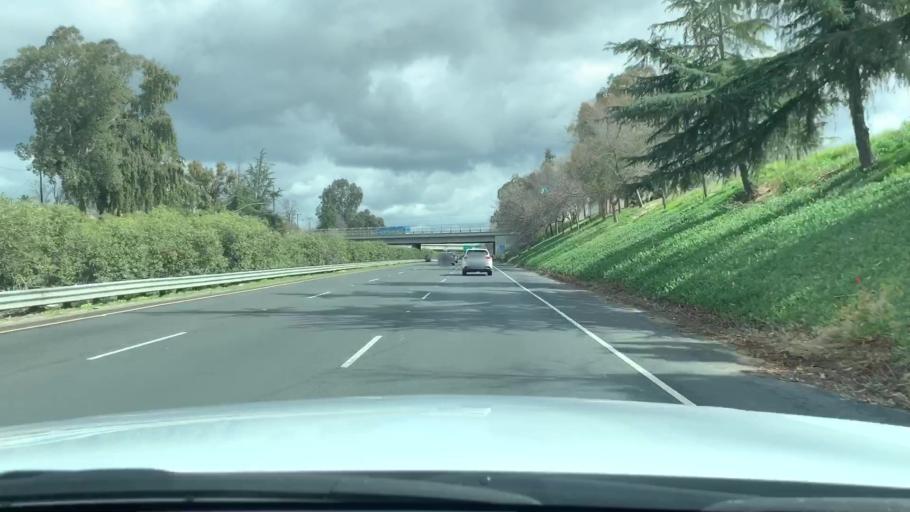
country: US
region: California
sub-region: Kern County
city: Bakersfield
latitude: 35.3844
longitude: -118.9920
